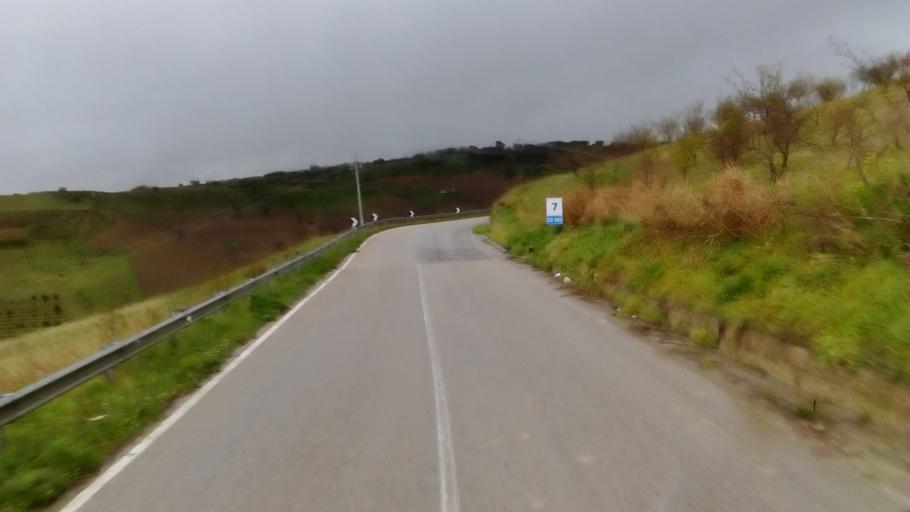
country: IT
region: Sicily
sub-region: Enna
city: Pietraperzia
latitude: 37.4415
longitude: 14.1769
